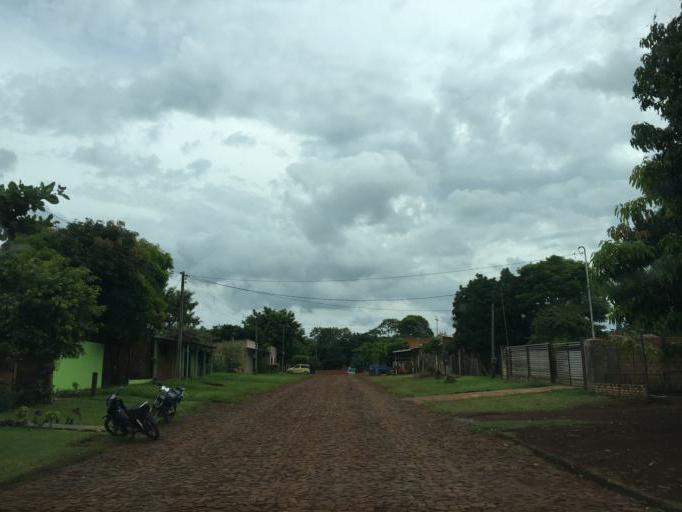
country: PY
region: Alto Parana
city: Ciudad del Este
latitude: -25.4231
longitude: -54.6455
